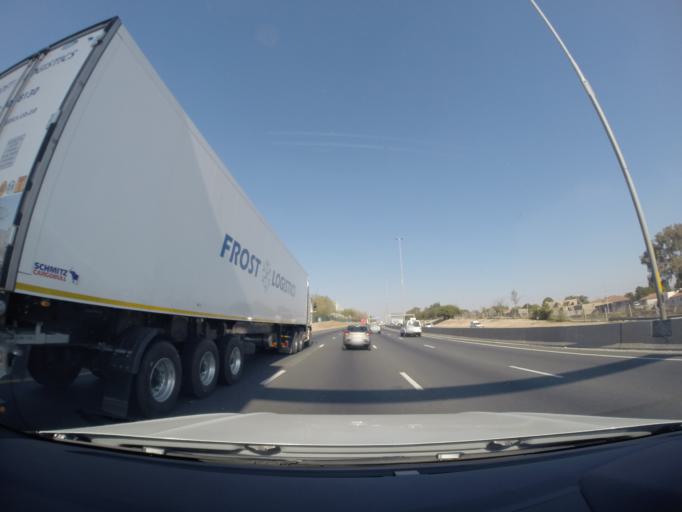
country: ZA
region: Gauteng
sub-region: City of Johannesburg Metropolitan Municipality
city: Modderfontein
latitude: -26.0850
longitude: 28.1192
